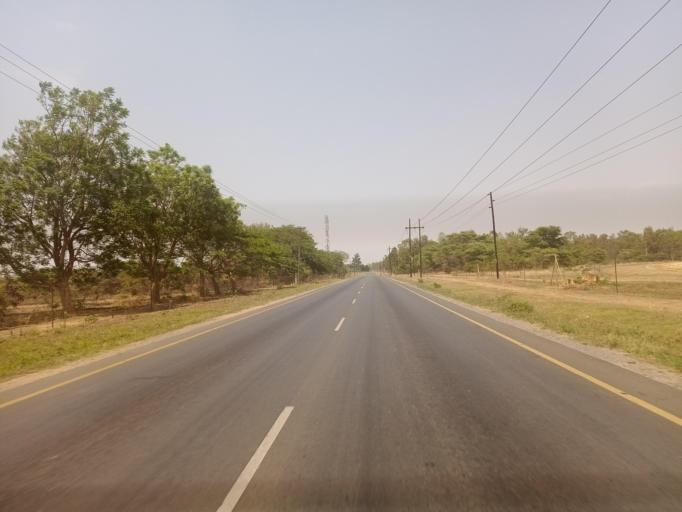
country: ZM
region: Lusaka
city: Lusaka
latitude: -15.2846
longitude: 28.3843
